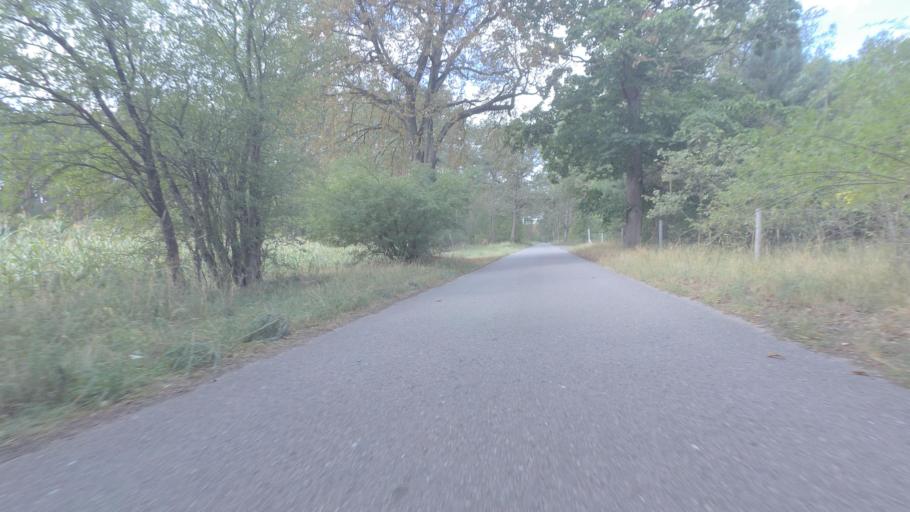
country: DE
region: Brandenburg
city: Wittstock
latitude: 53.0779
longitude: 12.4938
